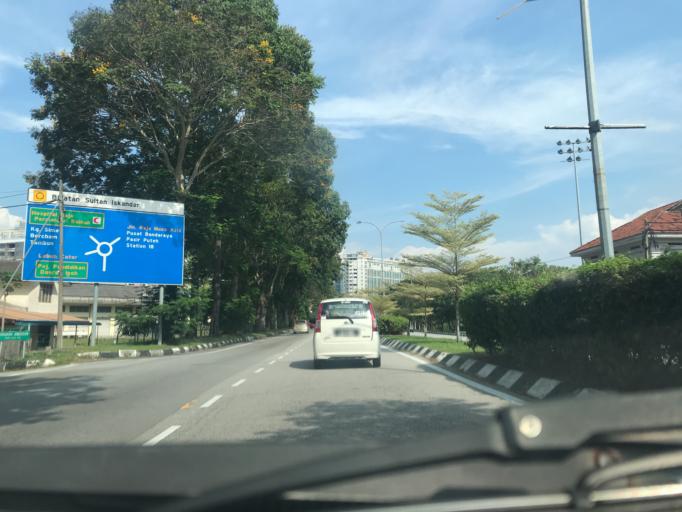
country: MY
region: Perak
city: Ipoh
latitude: 4.6056
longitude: 101.0856
